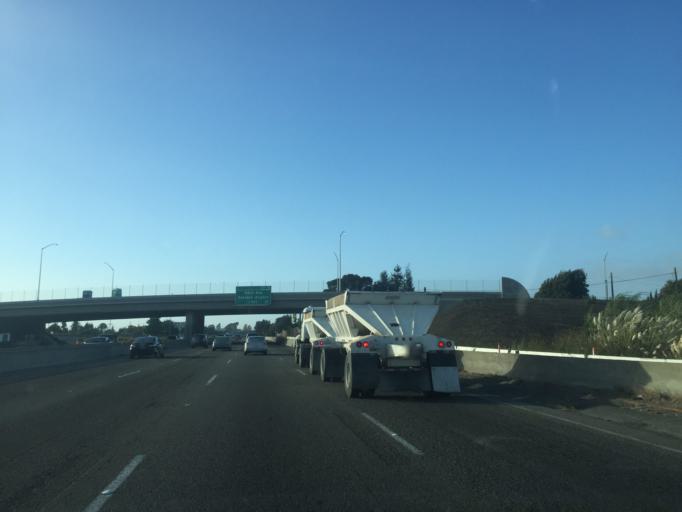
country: US
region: California
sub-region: Alameda County
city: San Leandro
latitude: 37.7182
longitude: -122.1756
